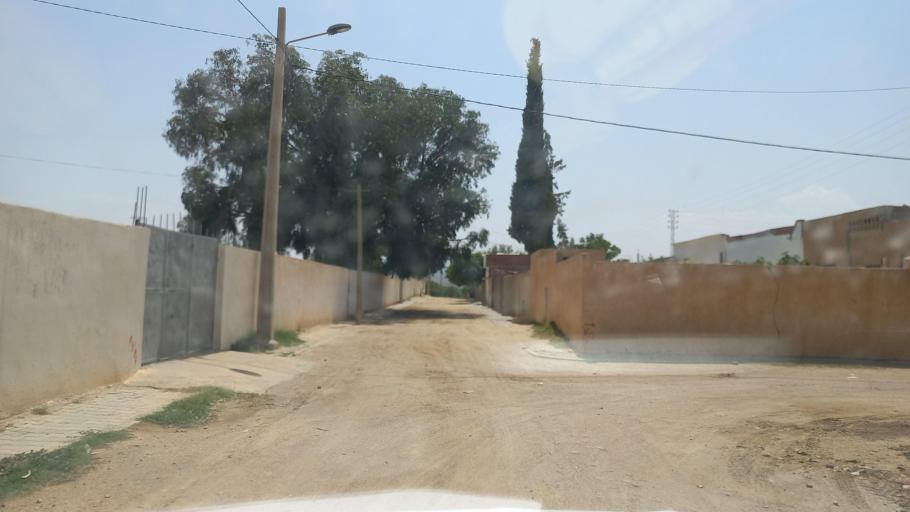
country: TN
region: Al Qasrayn
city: Kasserine
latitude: 35.2505
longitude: 9.0272
